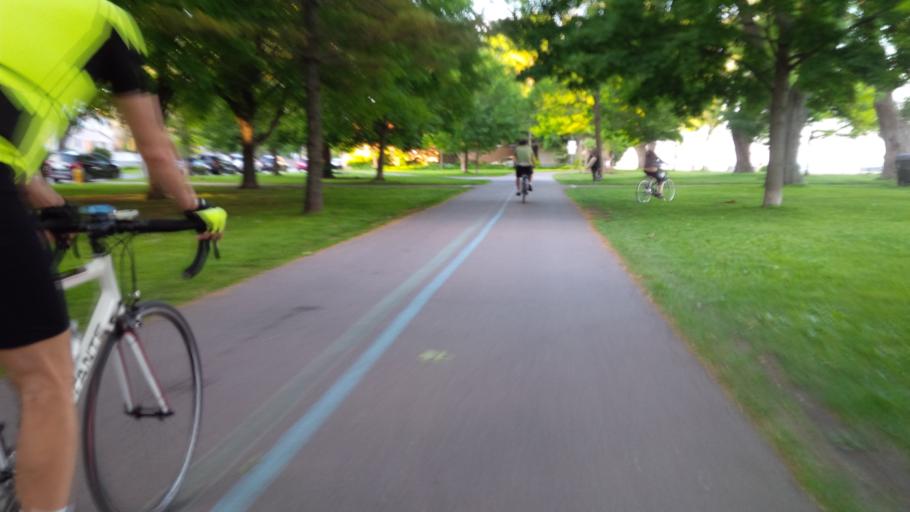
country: CA
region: Ontario
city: Scarborough
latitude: 43.6672
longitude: -79.2956
